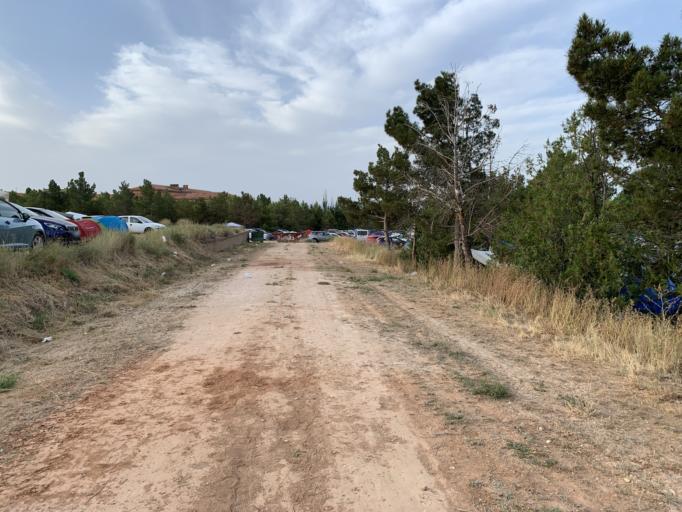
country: ES
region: Aragon
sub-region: Provincia de Teruel
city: Teruel
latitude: 40.3502
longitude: -1.1147
